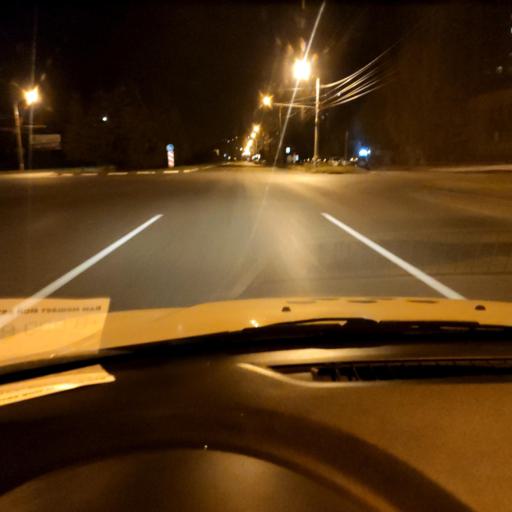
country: RU
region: Samara
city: Tol'yatti
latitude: 53.5072
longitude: 49.4445
